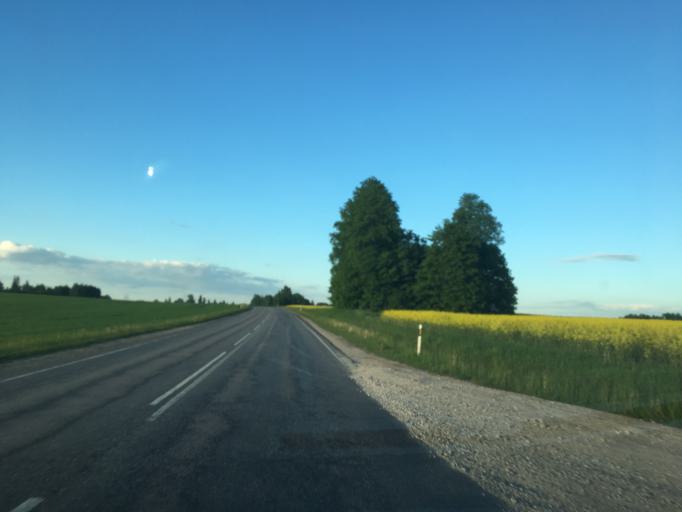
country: EE
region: Tartu
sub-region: Noo vald
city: Noo
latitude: 58.2161
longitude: 26.6142
